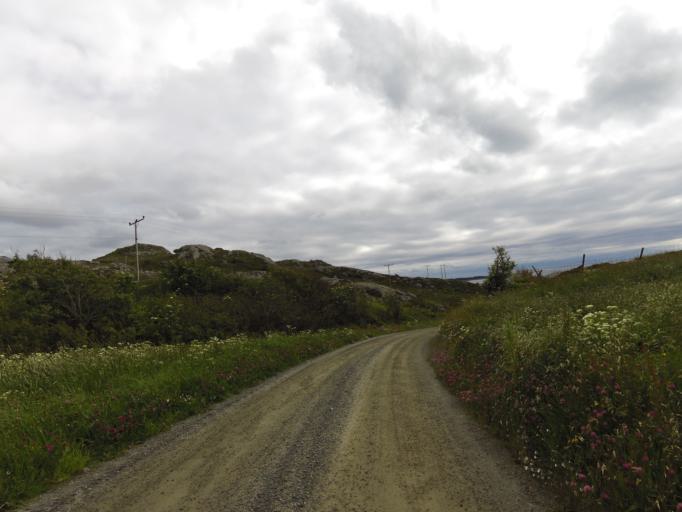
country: NO
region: Vest-Agder
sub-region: Farsund
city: Vestbygd
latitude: 58.1495
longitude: 6.6172
